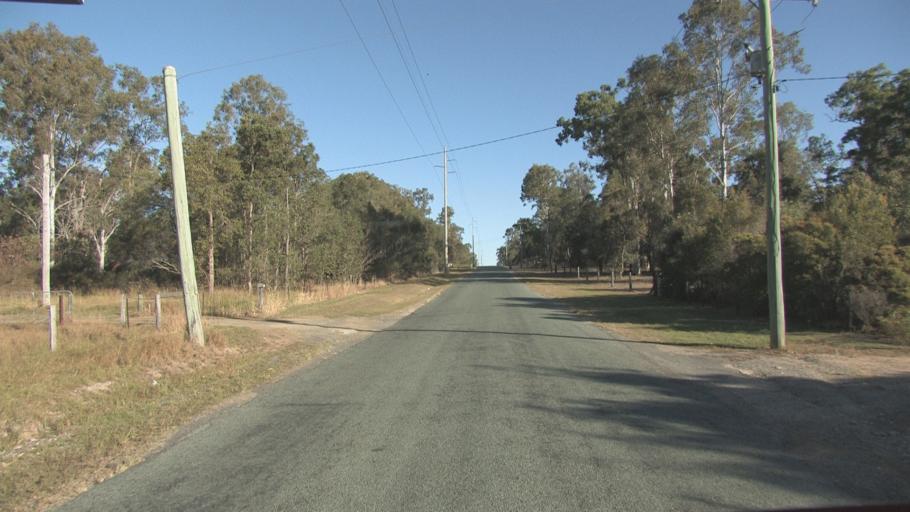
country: AU
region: Queensland
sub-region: Logan
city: North Maclean
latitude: -27.7947
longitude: 153.0424
